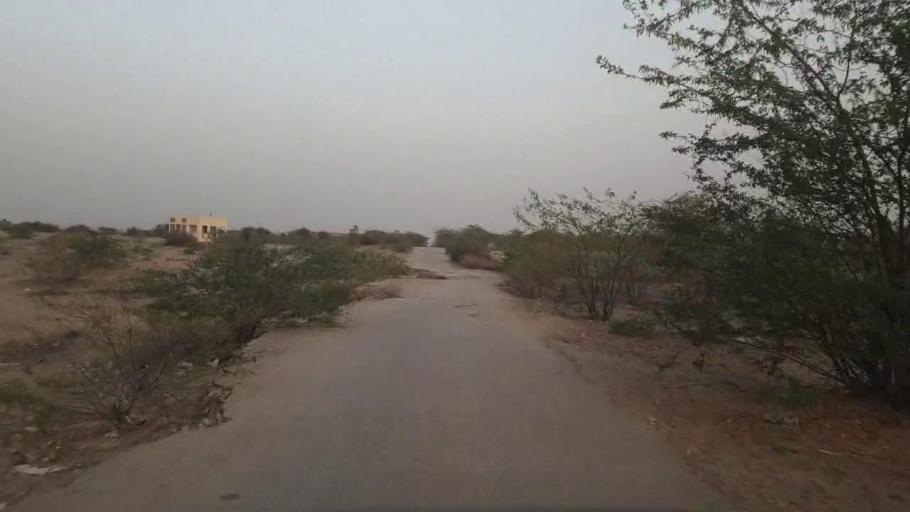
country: PK
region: Sindh
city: Chor
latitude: 25.5153
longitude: 69.8106
